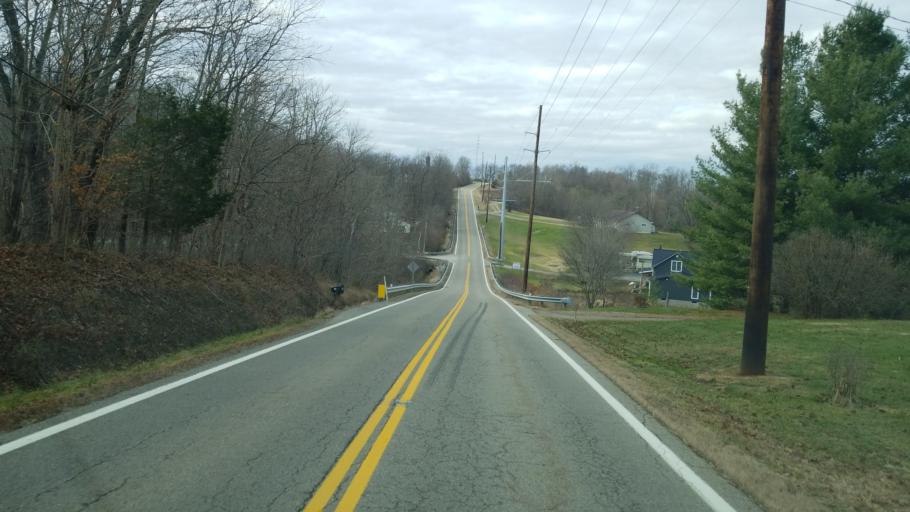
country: US
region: Ohio
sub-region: Ross County
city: Frankfort
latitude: 39.3466
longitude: -83.1806
